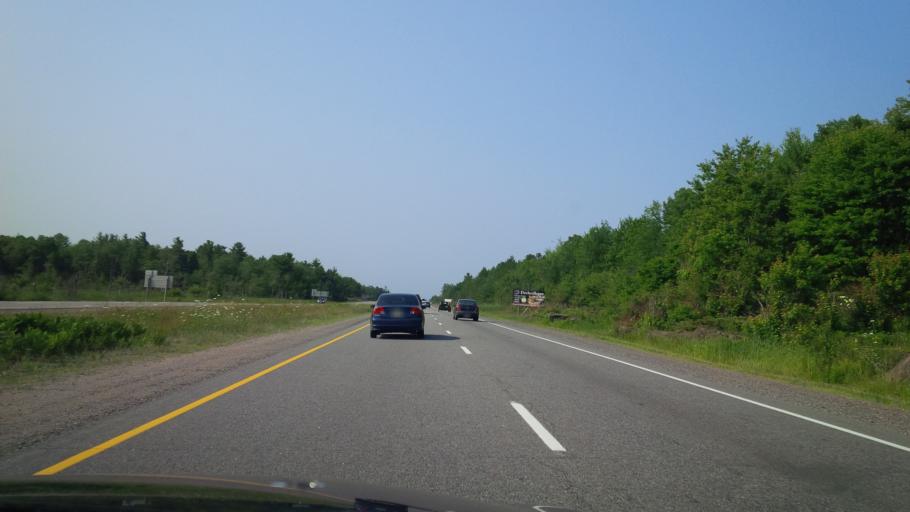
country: CA
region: Ontario
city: Bracebridge
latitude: 44.9749
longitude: -79.3181
